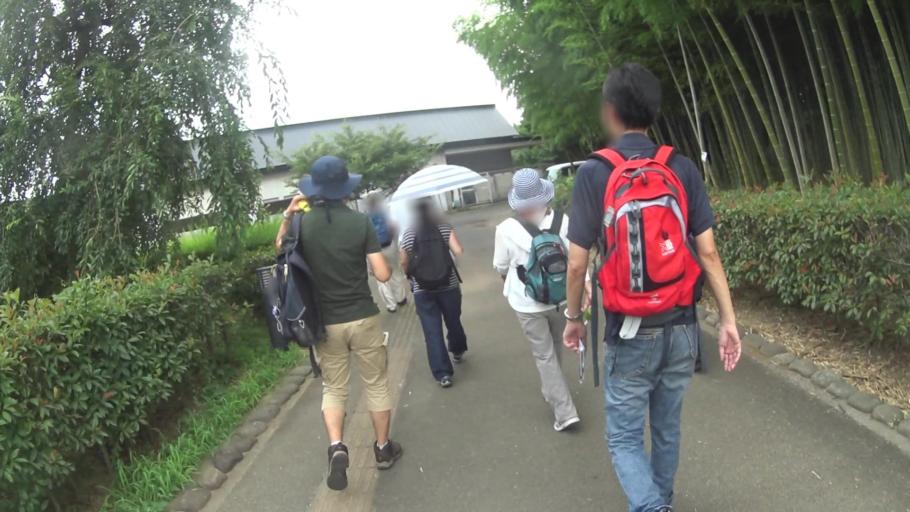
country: JP
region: Saitama
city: Okegawa
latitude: 35.9604
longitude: 139.5492
